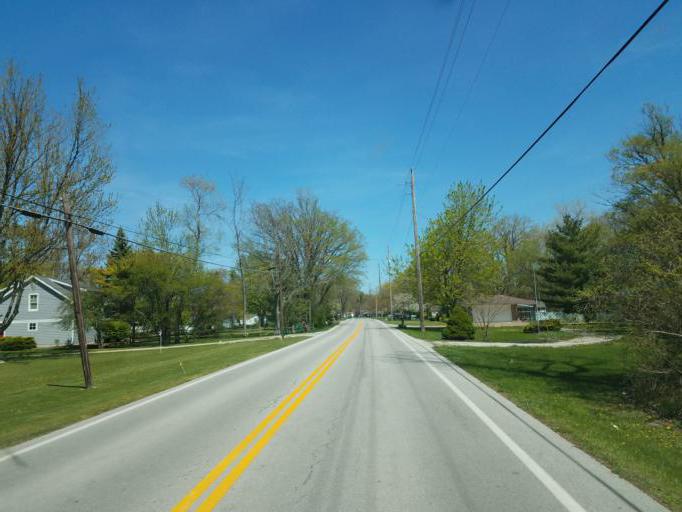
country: US
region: Ohio
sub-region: Ottawa County
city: Port Clinton
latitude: 41.5297
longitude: -82.8726
